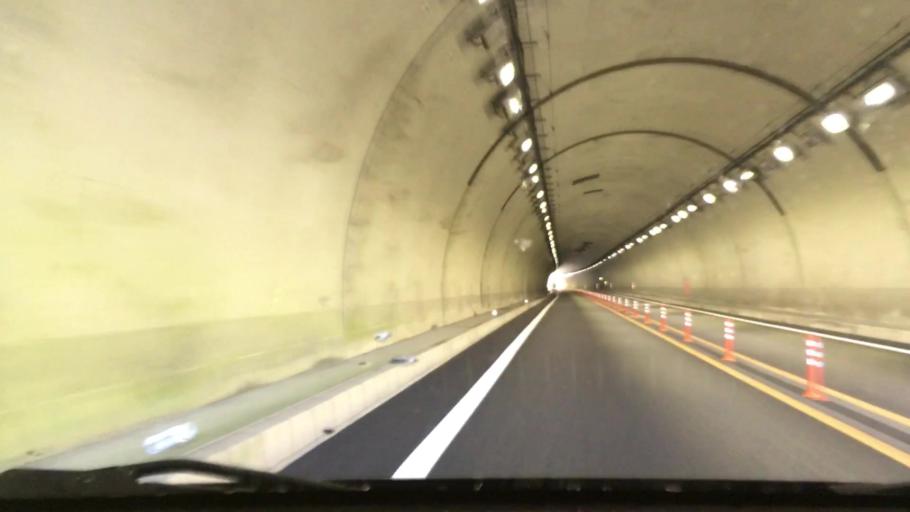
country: JP
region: Kagoshima
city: Kokubu-matsuki
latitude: 31.7312
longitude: 130.8379
